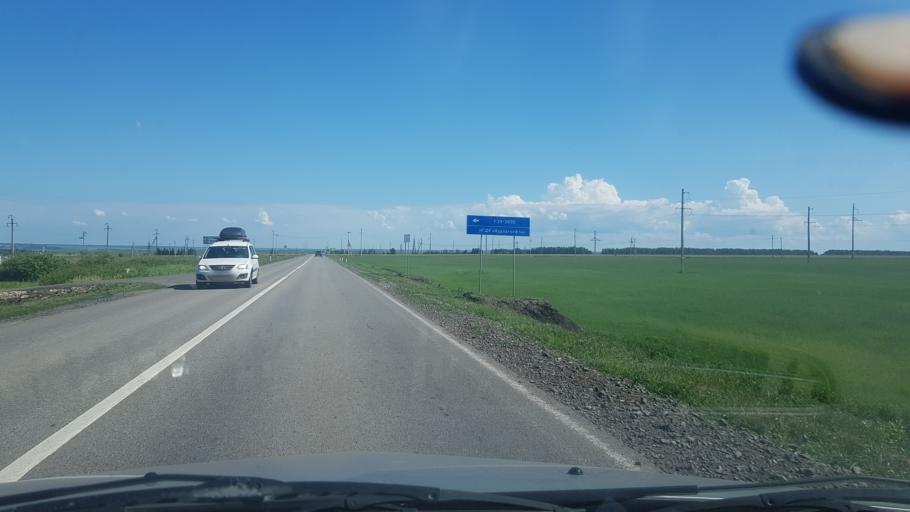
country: RU
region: Tatarstan
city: Nurlat
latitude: 54.4705
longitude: 50.8382
